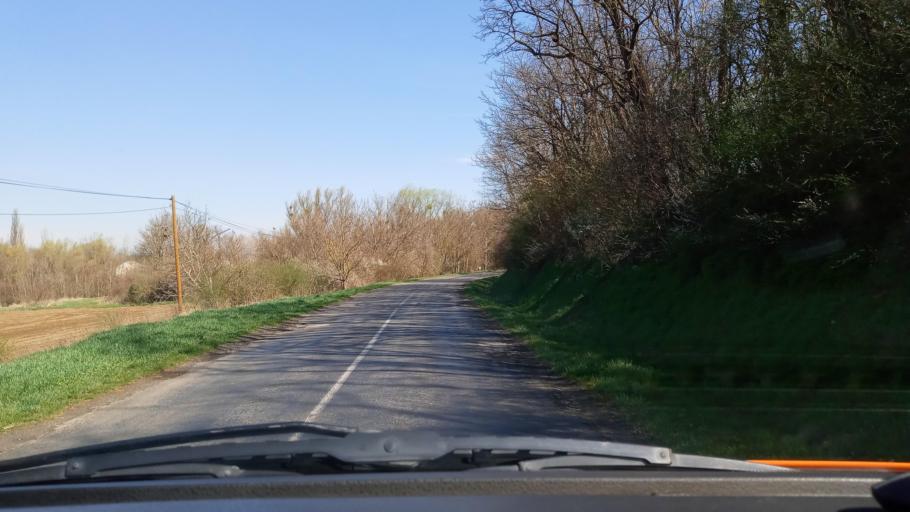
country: HU
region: Baranya
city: Boly
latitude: 46.0196
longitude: 18.4561
